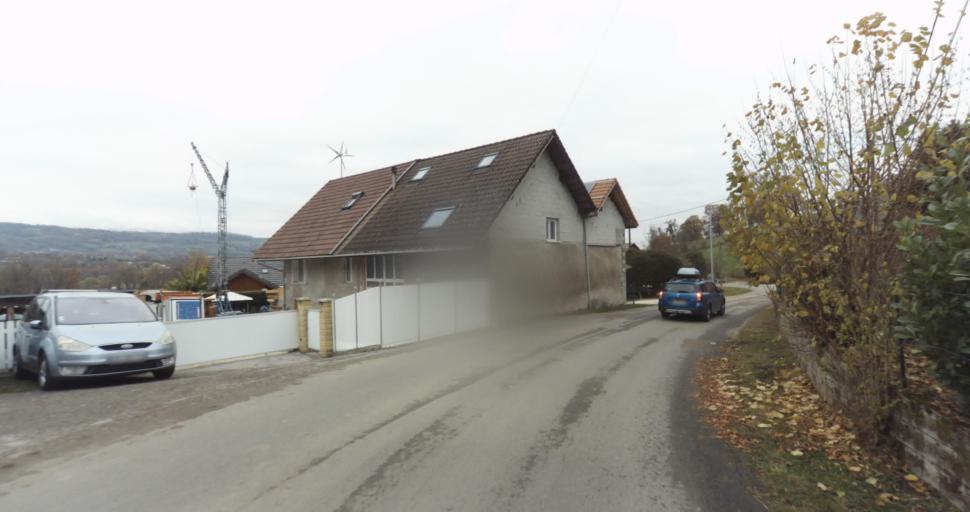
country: FR
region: Rhone-Alpes
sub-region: Departement de la Savoie
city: Albens
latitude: 45.7672
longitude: 5.9652
